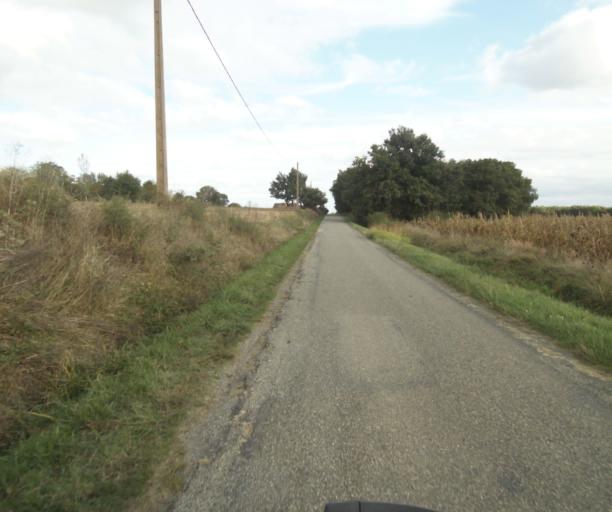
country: FR
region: Midi-Pyrenees
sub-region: Departement du Tarn-et-Garonne
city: Verdun-sur-Garonne
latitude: 43.8401
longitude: 1.1310
